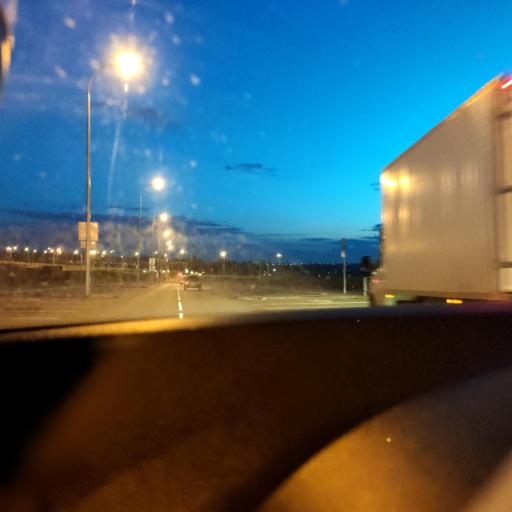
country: RU
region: Samara
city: Petra-Dubrava
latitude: 53.2972
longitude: 50.3289
